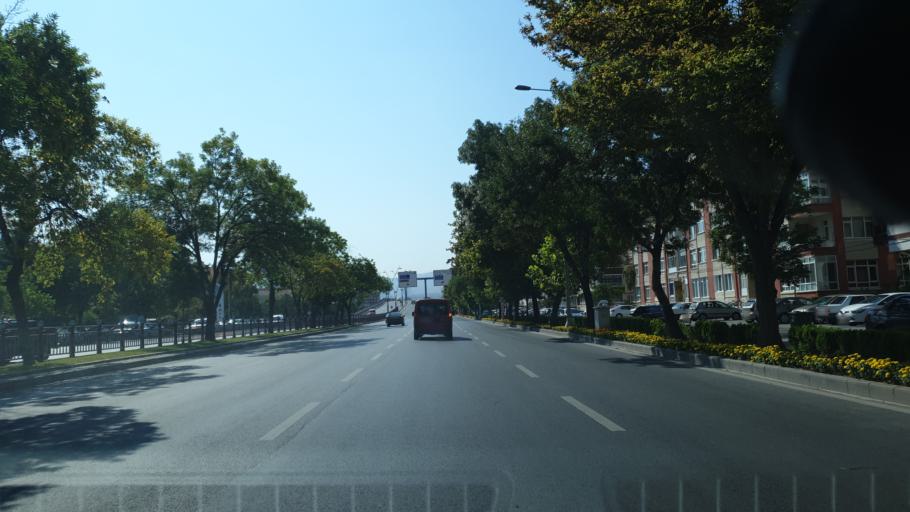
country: TR
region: Kayseri
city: Kayseri
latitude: 38.7387
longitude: 35.4915
